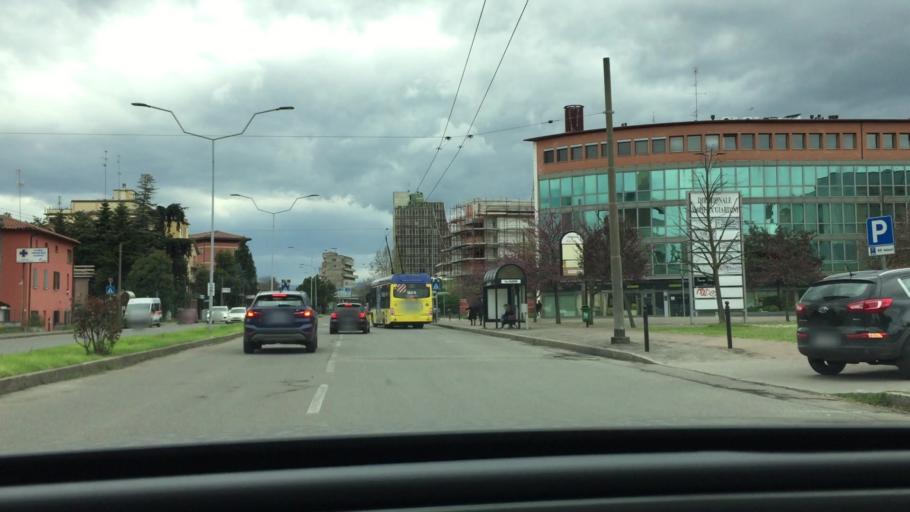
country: IT
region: Emilia-Romagna
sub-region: Provincia di Modena
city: Modena
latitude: 44.6382
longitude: 10.9058
